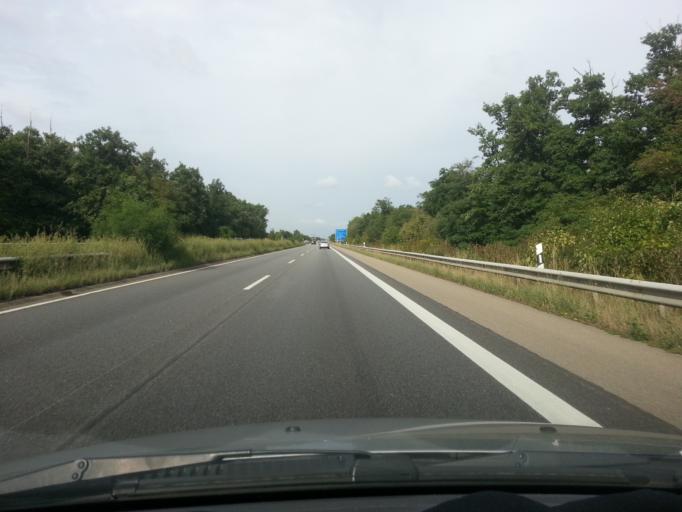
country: DE
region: Rheinland-Pfalz
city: Lachen-Speyerdorf
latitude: 49.3516
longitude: 8.1939
